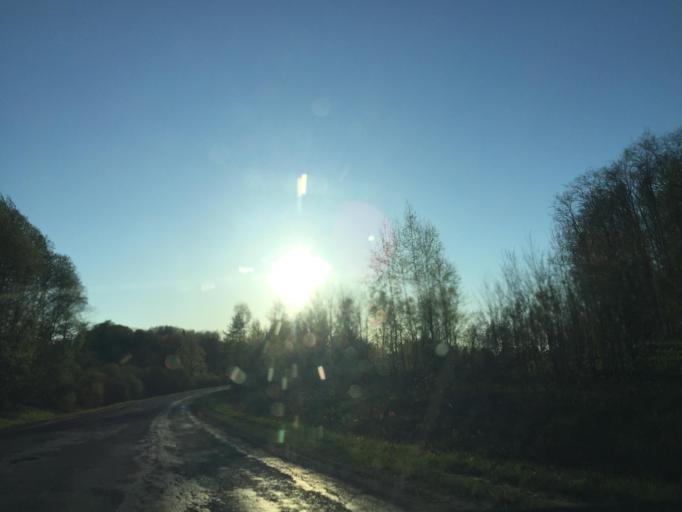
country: LV
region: Ergli
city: Ergli
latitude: 56.8757
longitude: 25.6955
